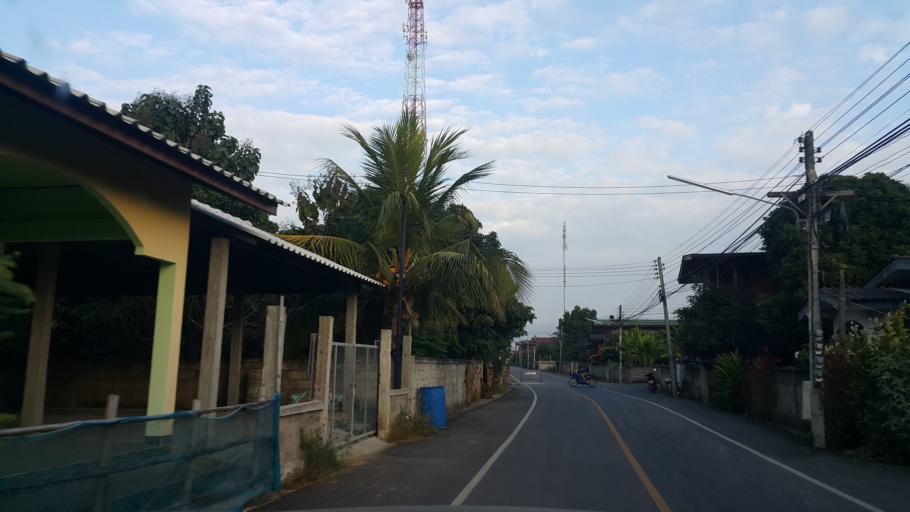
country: TH
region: Lampang
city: Sop Prap
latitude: 17.8903
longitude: 99.3351
